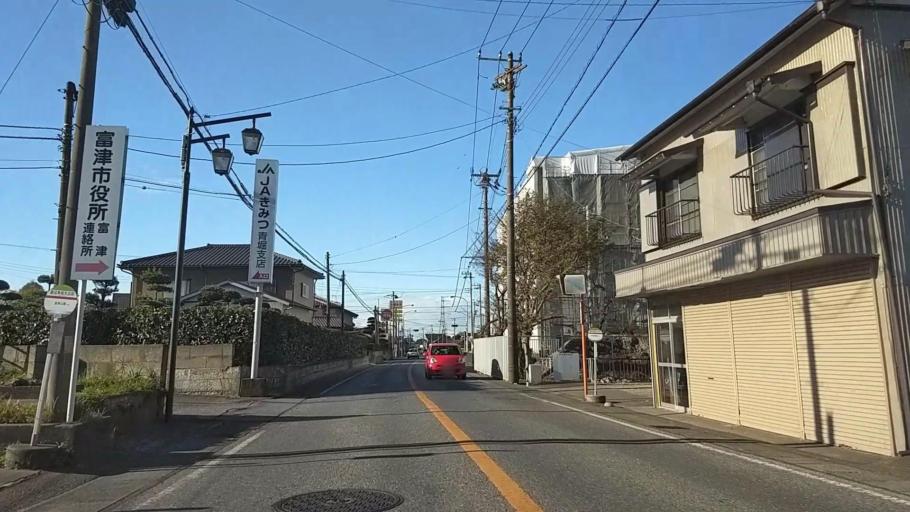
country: JP
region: Chiba
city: Futtsu
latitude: 35.3246
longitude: 139.8465
